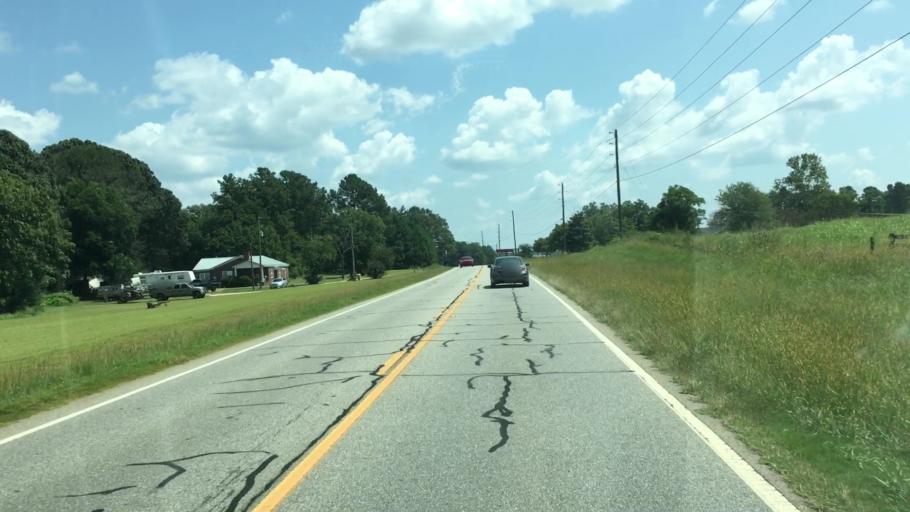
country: US
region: Georgia
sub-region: Barrow County
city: Statham
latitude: 33.9460
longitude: -83.6474
